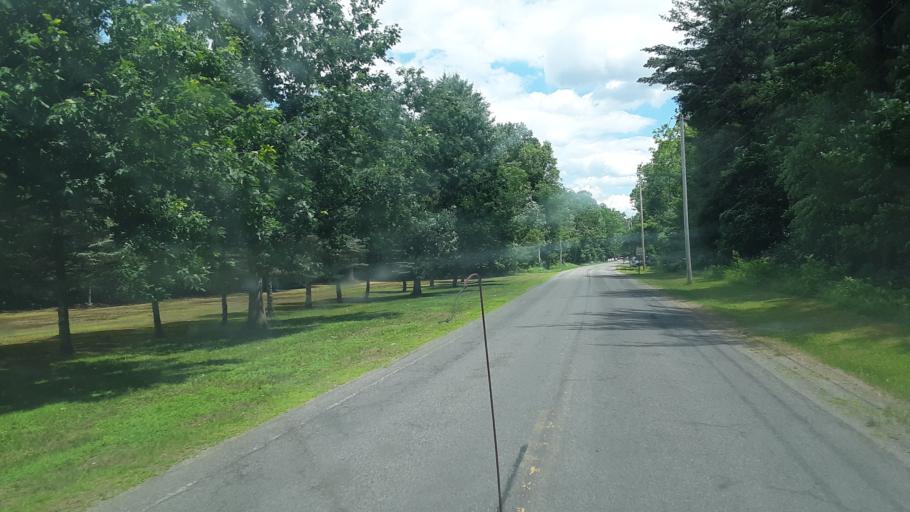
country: US
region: New York
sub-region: Oneida County
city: Rome
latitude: 43.2632
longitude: -75.5692
